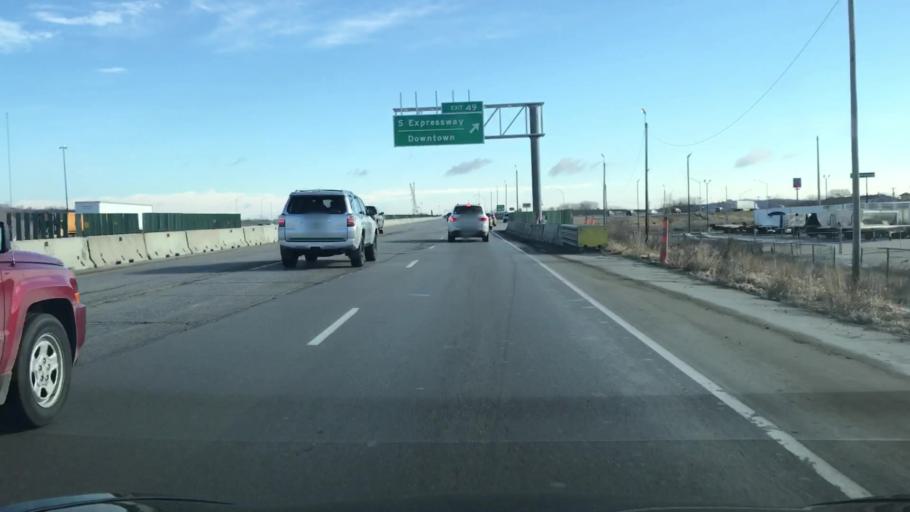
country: US
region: Iowa
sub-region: Pottawattamie County
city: Council Bluffs
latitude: 41.2320
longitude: -95.8581
